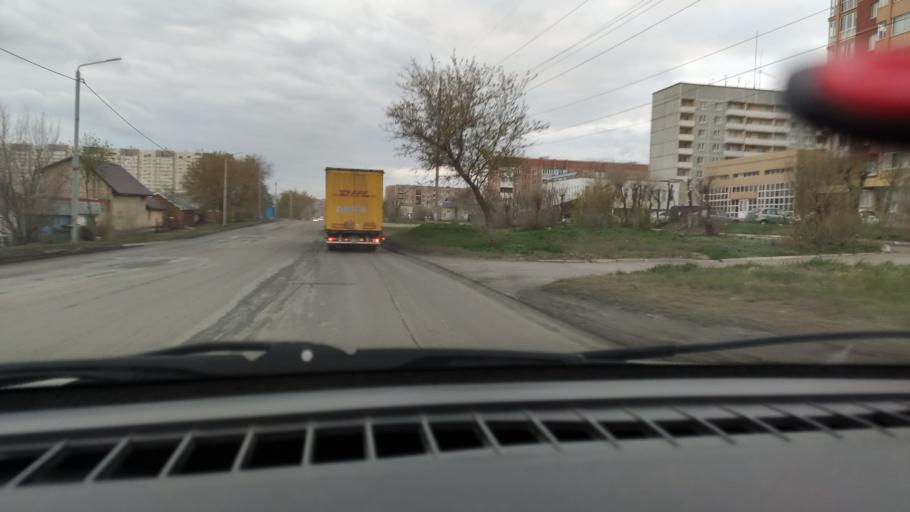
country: RU
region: Orenburg
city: Orenburg
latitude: 51.7858
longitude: 55.1792
